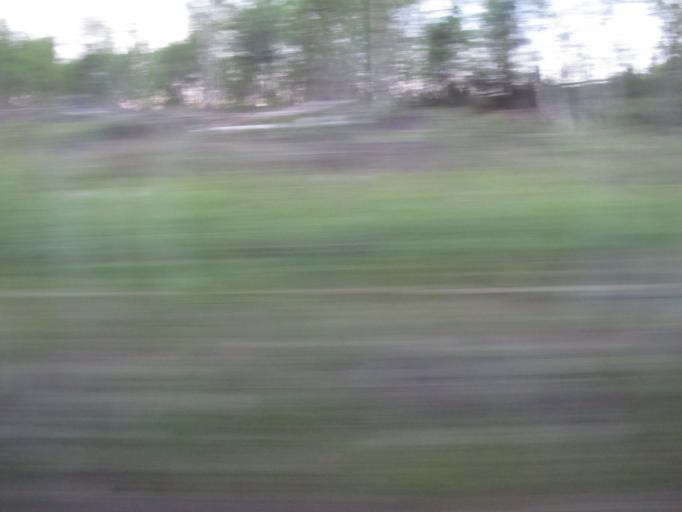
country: NO
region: Oppland
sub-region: Lillehammer
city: Lillehammer
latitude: 61.1891
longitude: 10.4144
